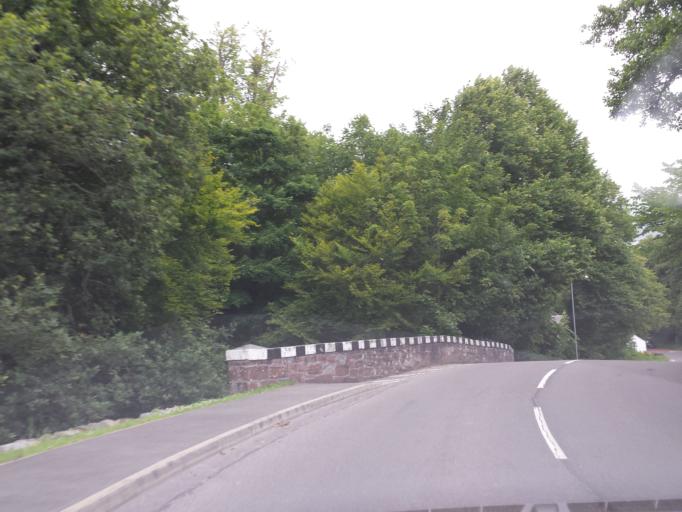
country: GB
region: Scotland
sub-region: Dumfries and Galloway
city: Dumfries
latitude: 54.9803
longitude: -3.6232
